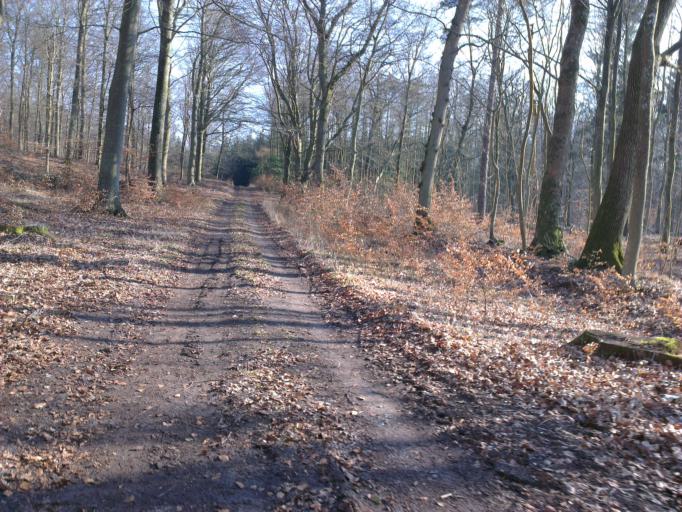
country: DK
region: Capital Region
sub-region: Frederikssund Kommune
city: Jaegerspris
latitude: 55.8952
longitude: 11.9990
